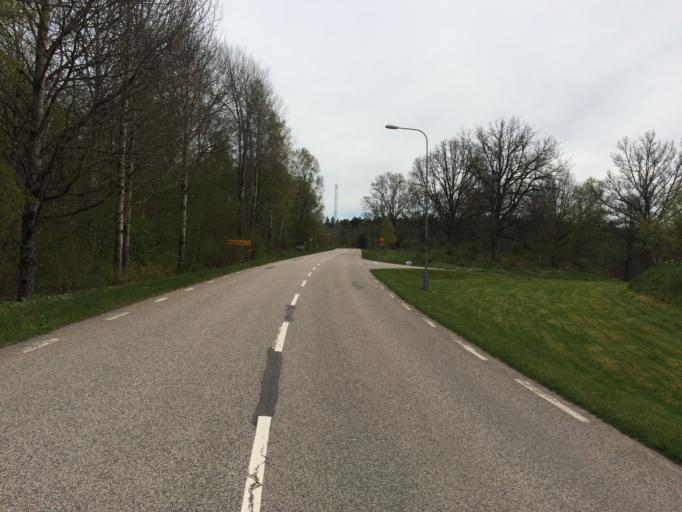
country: SE
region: Vaestra Goetaland
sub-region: Ulricehamns Kommun
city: Ulricehamn
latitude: 57.7332
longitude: 13.4309
